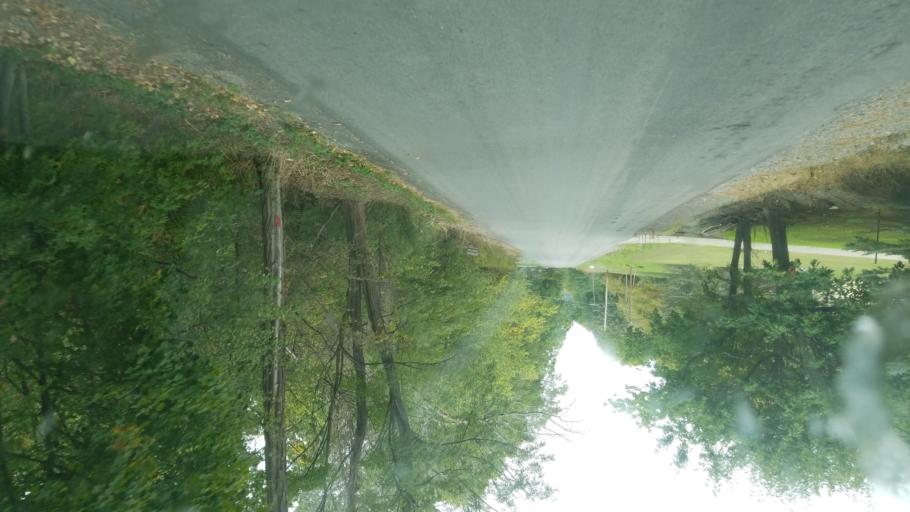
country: US
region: Pennsylvania
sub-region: Mercer County
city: Stoneboro
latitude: 41.4012
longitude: -80.2367
